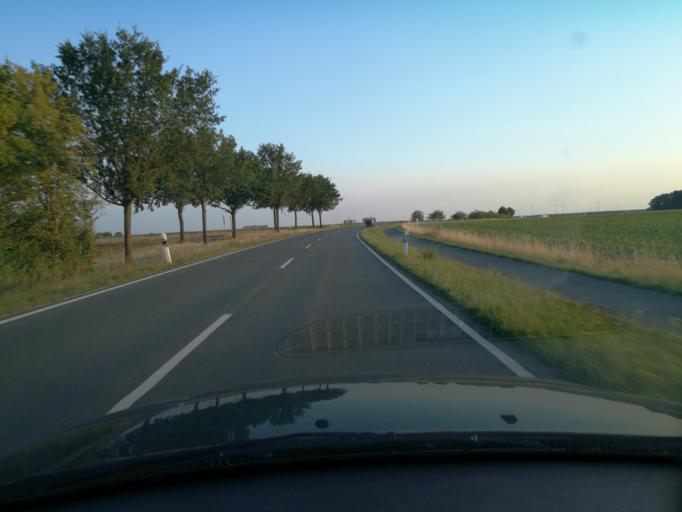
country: DE
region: Bavaria
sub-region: Regierungsbezirk Mittelfranken
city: Herzogenaurach
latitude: 49.5877
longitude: 10.8906
